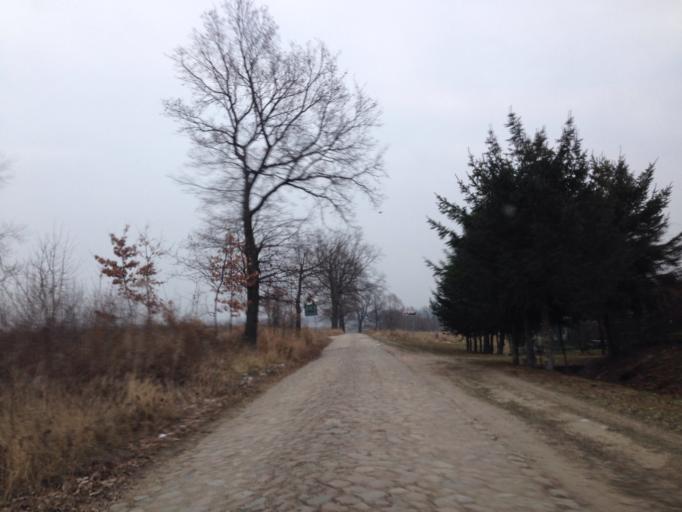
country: PL
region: Warmian-Masurian Voivodeship
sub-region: Powiat ketrzynski
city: Reszel
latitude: 54.1032
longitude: 21.2541
